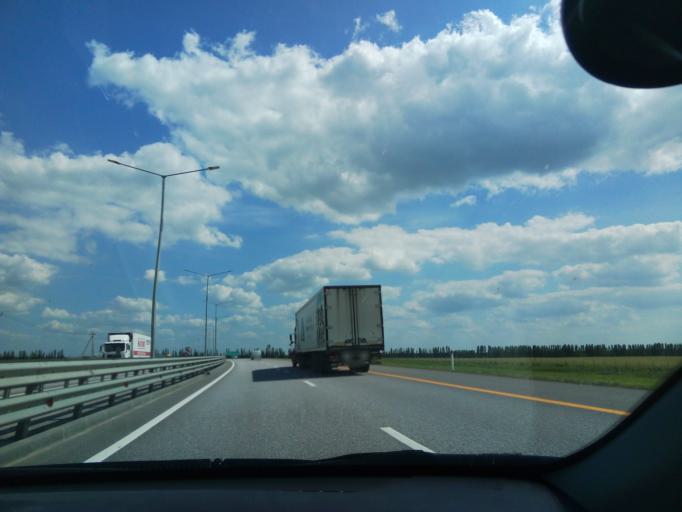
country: RU
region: Voronezj
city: Kashirskoye
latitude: 51.4872
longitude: 39.5339
